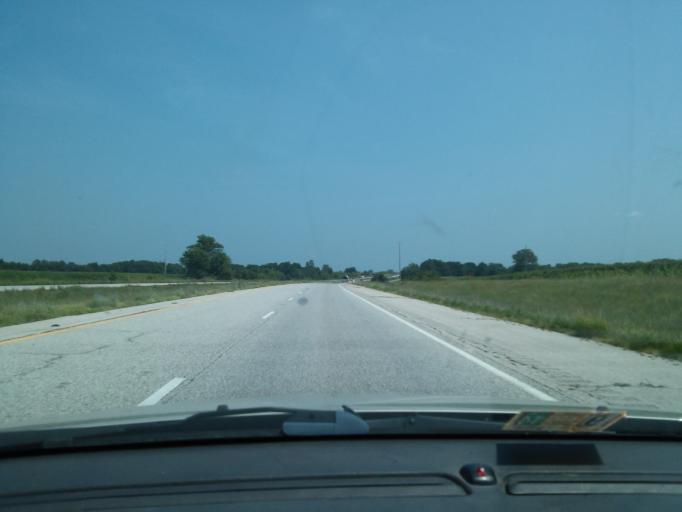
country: US
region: Illinois
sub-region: Pike County
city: Griggsville
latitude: 39.6777
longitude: -90.7267
